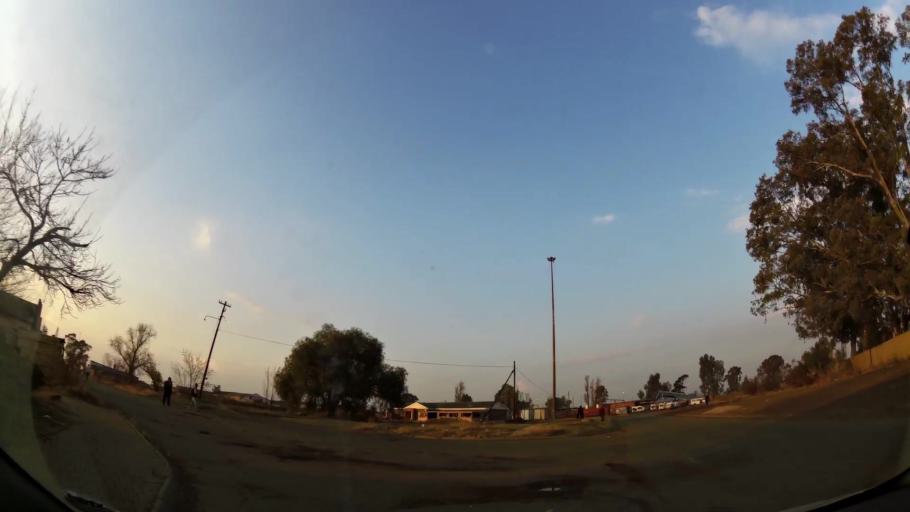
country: ZA
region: Gauteng
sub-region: City of Johannesburg Metropolitan Municipality
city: Orange Farm
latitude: -26.5387
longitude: 27.8858
